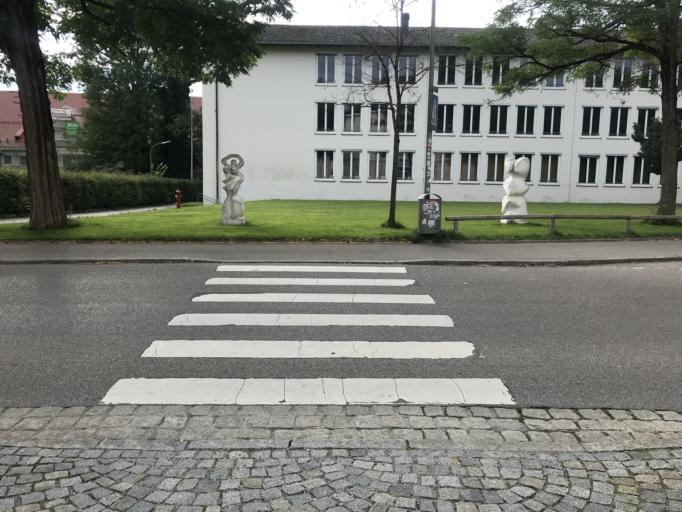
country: DE
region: Bavaria
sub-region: Upper Bavaria
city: Landsberg am Lech
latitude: 48.0518
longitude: 10.8744
